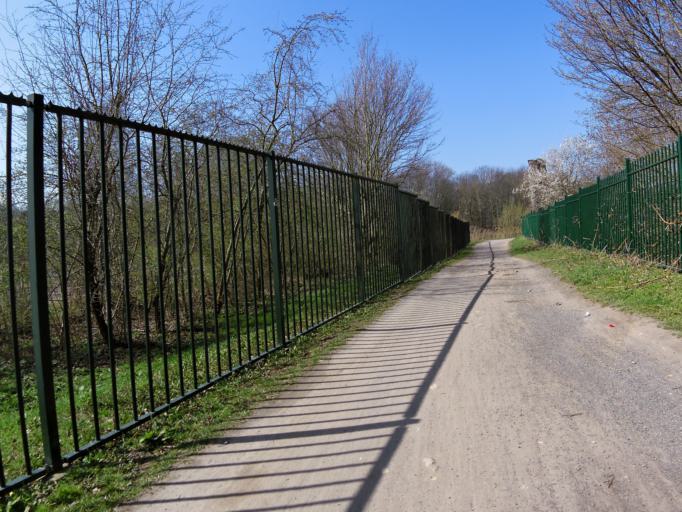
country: DE
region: Saxony
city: Leipzig
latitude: 51.3563
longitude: 12.3386
